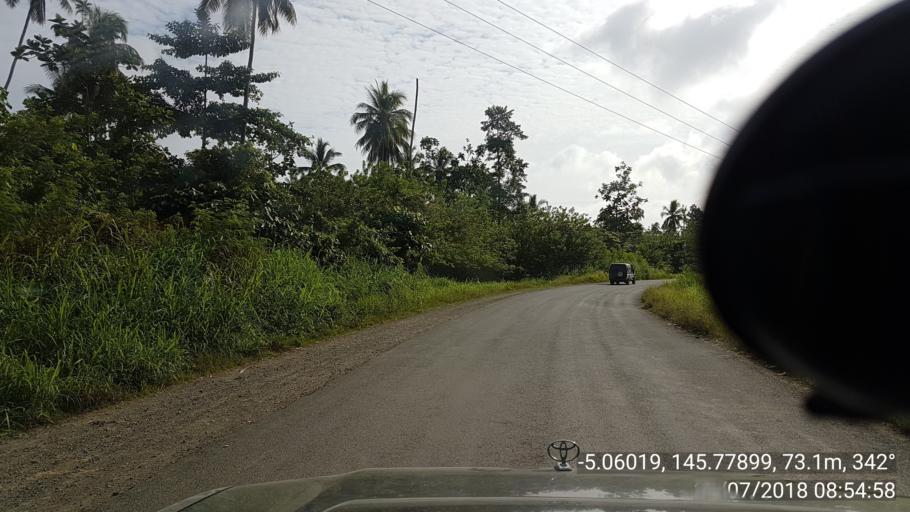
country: PG
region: Madang
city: Madang
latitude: -5.0603
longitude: 145.7789
